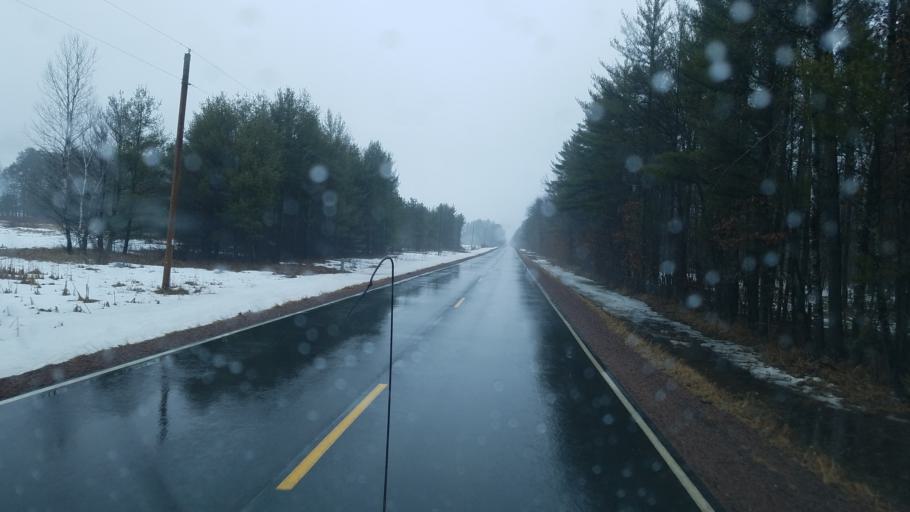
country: US
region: Wisconsin
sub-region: Wood County
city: Marshfield
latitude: 44.5178
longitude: -90.2994
